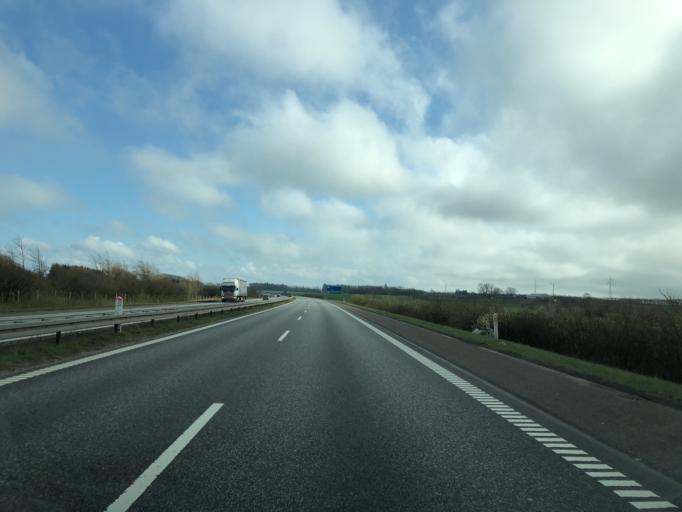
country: DK
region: North Denmark
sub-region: Hjorring Kommune
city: Vra
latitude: 57.3780
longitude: 10.0214
